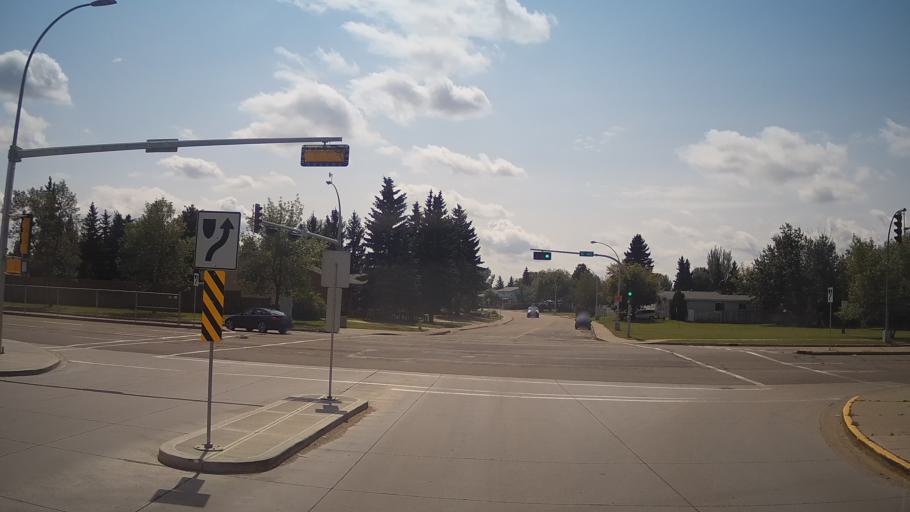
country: CA
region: Alberta
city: St. Albert
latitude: 53.5206
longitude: -113.6236
